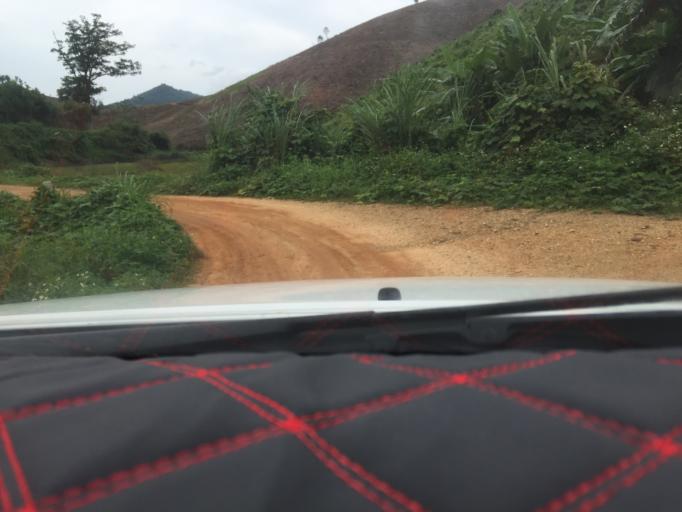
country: TH
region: Chiang Rai
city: Khun Tan
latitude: 19.7777
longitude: 100.4951
